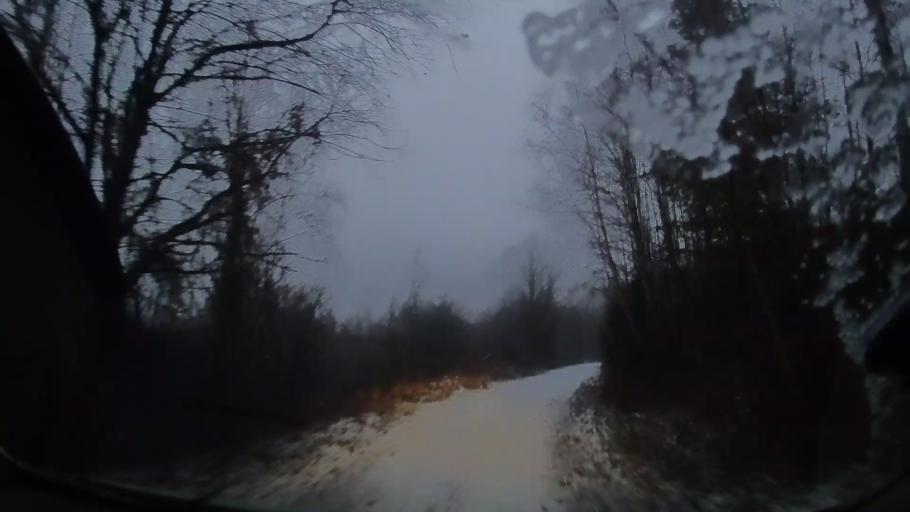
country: RO
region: Alba
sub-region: Comuna Avram Iancu
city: Avram Iancu
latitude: 46.3086
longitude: 22.7978
